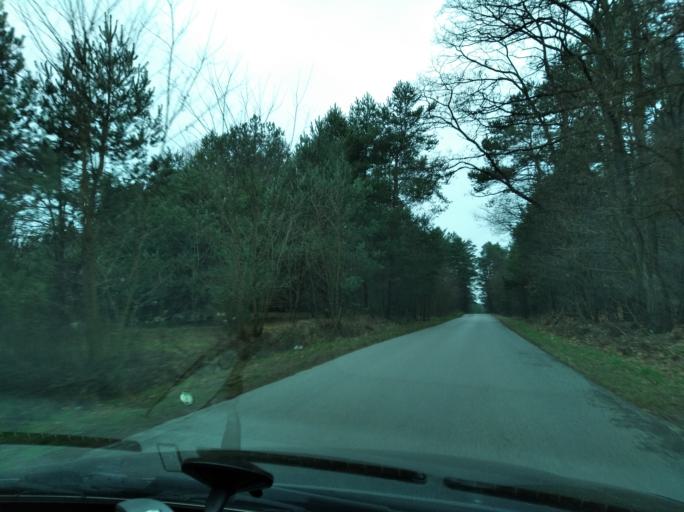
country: PL
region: Subcarpathian Voivodeship
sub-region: Powiat lancucki
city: Brzoza Stadnicka
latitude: 50.2028
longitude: 22.2778
